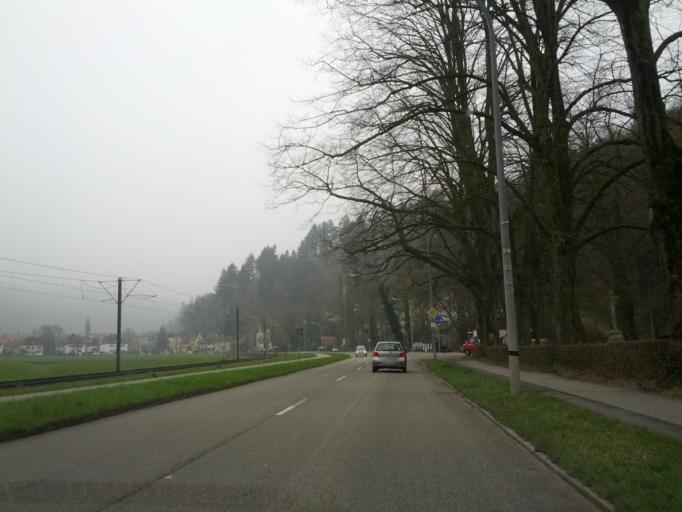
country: DE
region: Baden-Wuerttemberg
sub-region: Freiburg Region
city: Merzhausen
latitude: 47.9697
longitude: 7.8487
